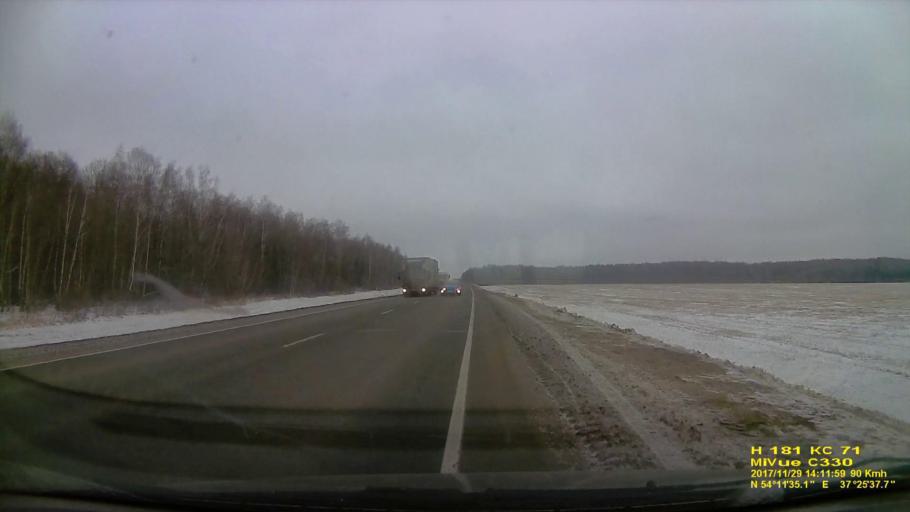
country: RU
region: Tula
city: Barsuki
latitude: 54.1929
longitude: 37.4274
